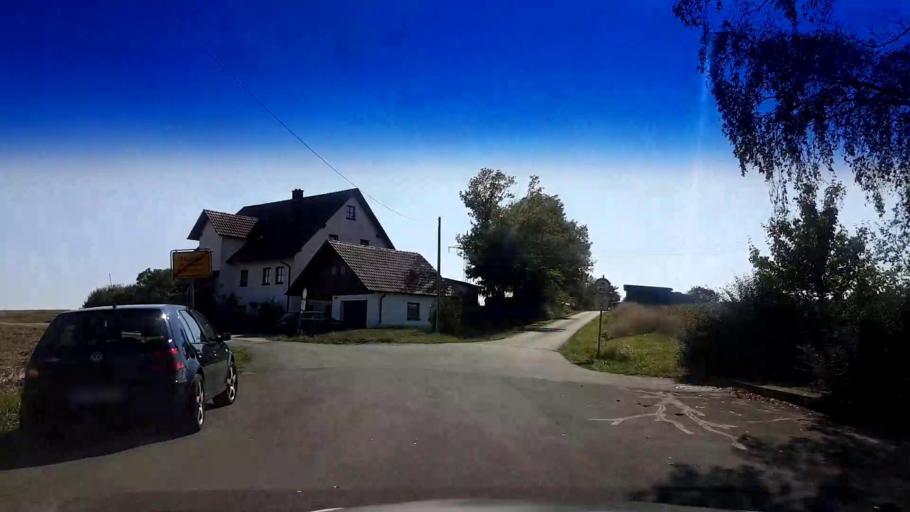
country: DE
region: Bavaria
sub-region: Upper Franconia
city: Litzendorf
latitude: 49.9059
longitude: 11.0018
